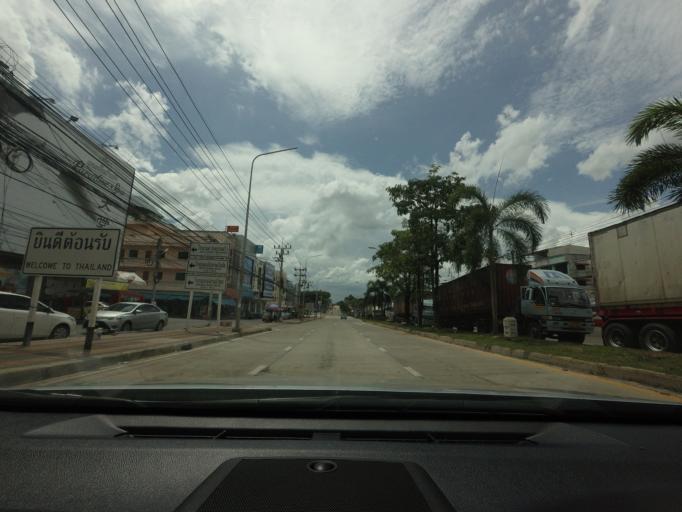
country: TH
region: Songkhla
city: Sadao
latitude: 6.5248
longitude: 100.4183
